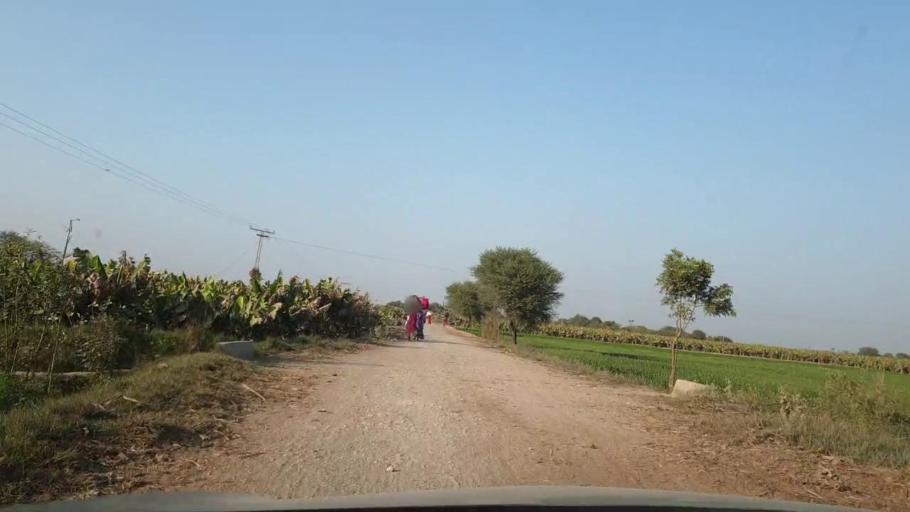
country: PK
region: Sindh
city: Tando Allahyar
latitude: 25.5788
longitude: 68.7801
